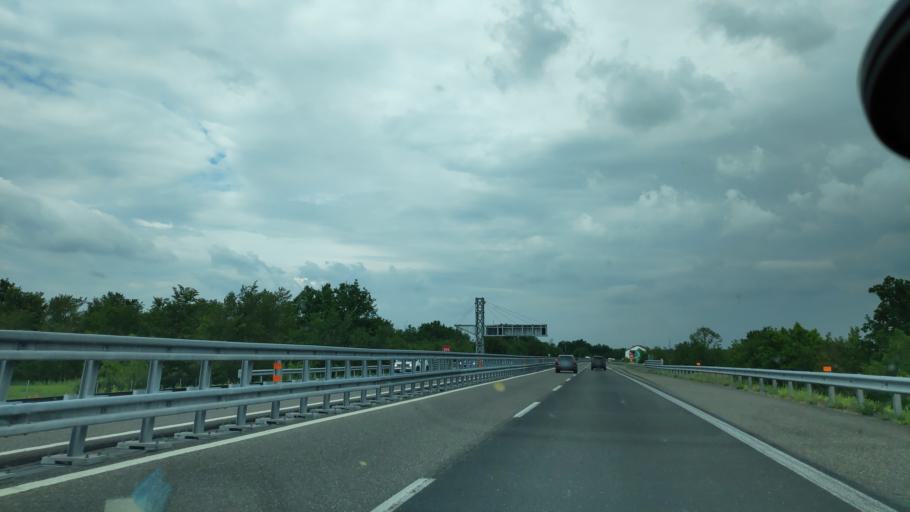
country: IT
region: Piedmont
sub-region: Provincia di Asti
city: Castello di Annone
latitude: 44.9090
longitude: 8.3214
